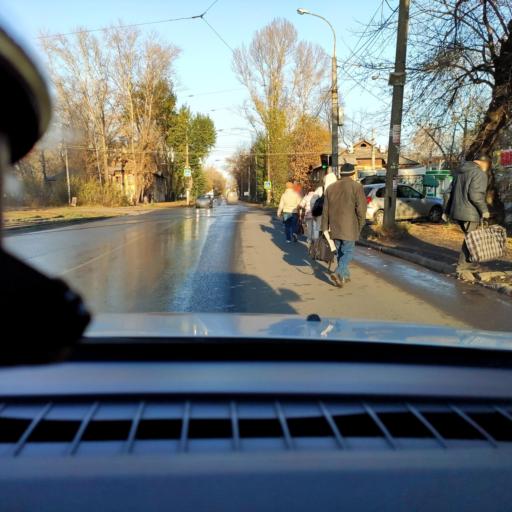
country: RU
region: Samara
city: Samara
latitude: 53.2344
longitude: 50.2596
